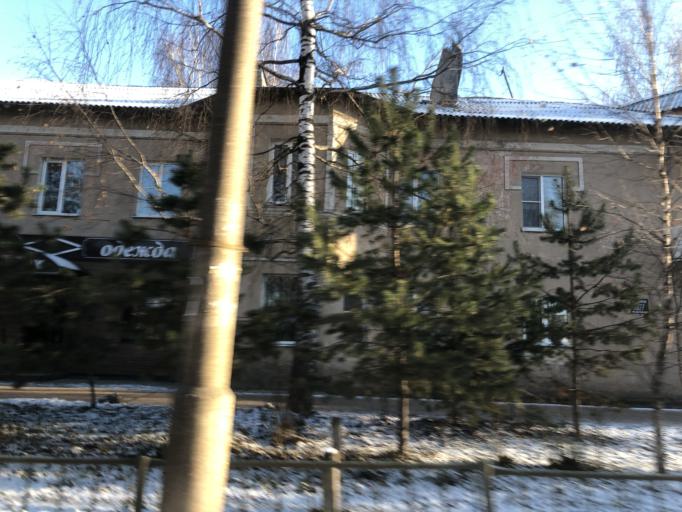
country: RU
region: Tverskaya
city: Rzhev
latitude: 56.2606
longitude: 34.3505
